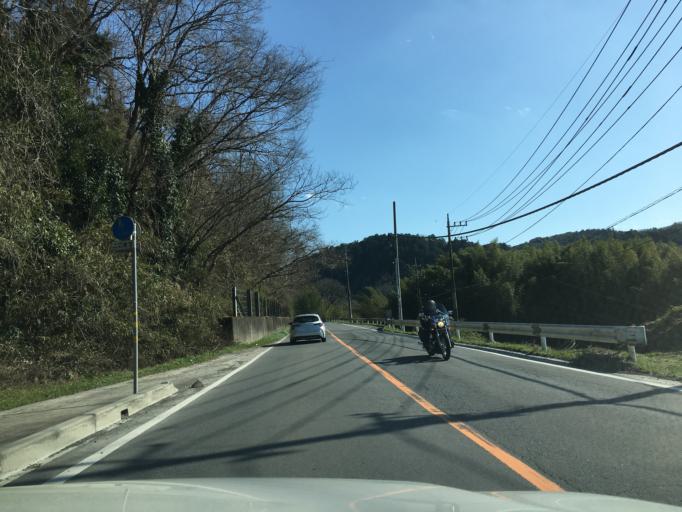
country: JP
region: Ibaraki
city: Omiya
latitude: 36.5545
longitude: 140.3219
